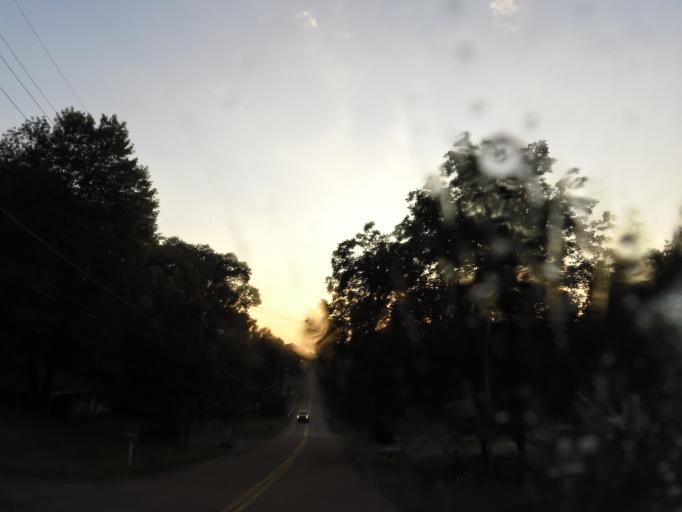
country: US
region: Tennessee
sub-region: Henry County
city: Paris
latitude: 36.2990
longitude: -88.3028
